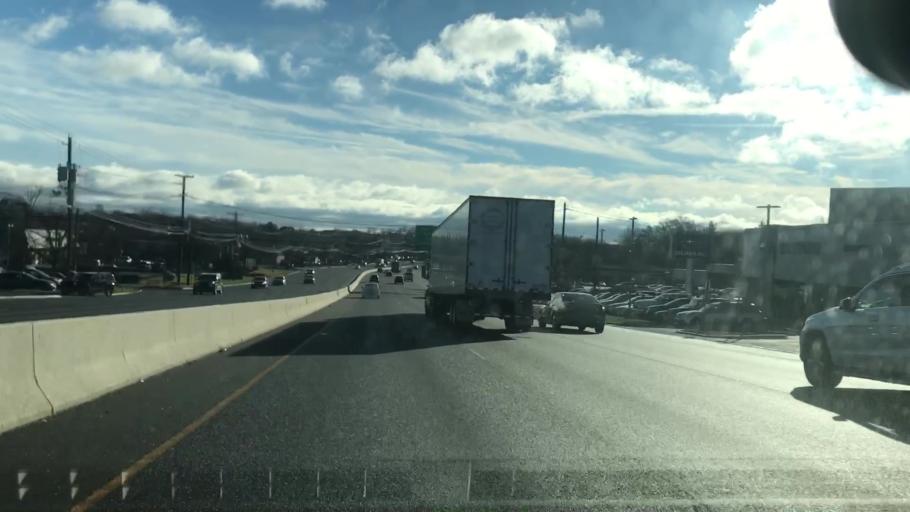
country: US
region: New Jersey
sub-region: Bergen County
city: Ramsey
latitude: 41.0648
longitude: -74.1299
